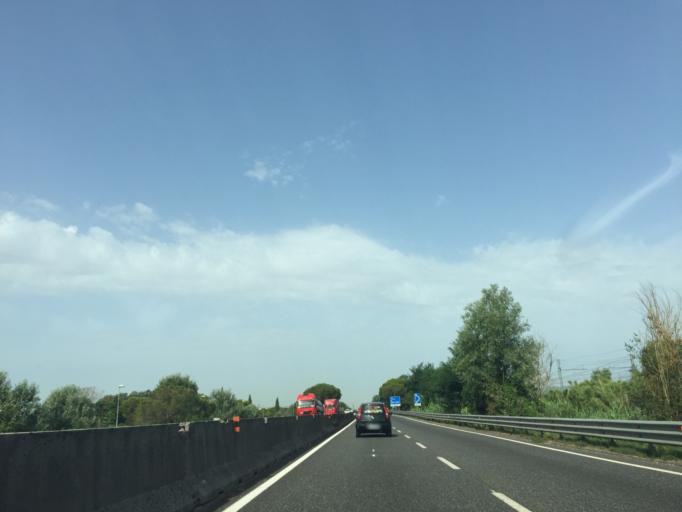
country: IT
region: Tuscany
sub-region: Province of Pisa
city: San Donato
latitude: 43.6977
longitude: 10.8036
